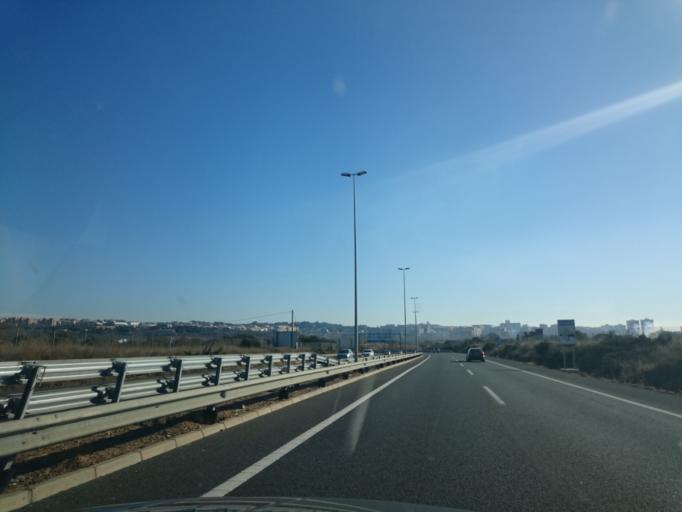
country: ES
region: Catalonia
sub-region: Provincia de Tarragona
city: Constanti
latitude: 41.1293
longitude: 1.2190
